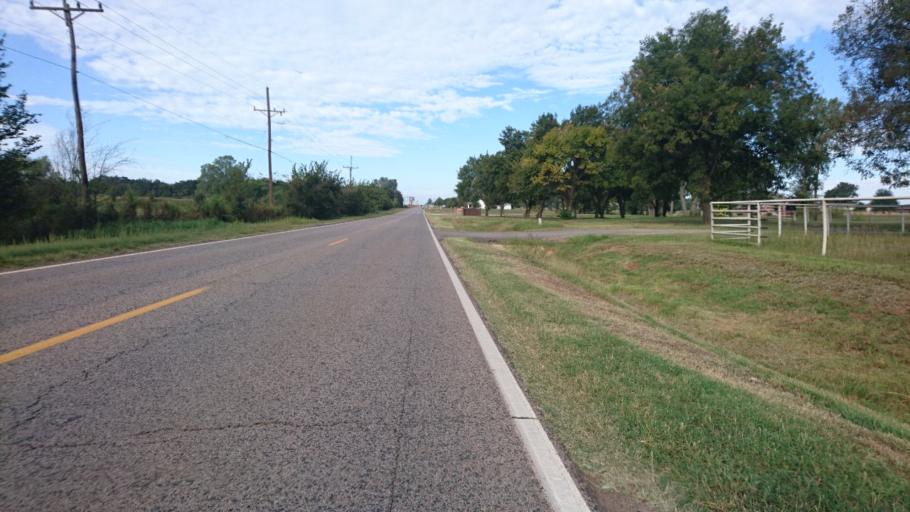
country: US
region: Oklahoma
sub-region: Lincoln County
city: Chandler
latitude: 35.6811
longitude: -97.0309
